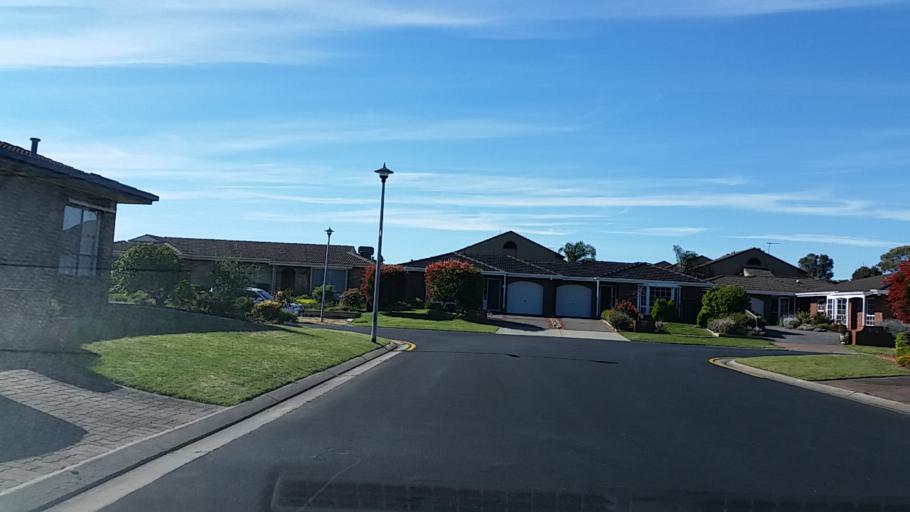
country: AU
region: South Australia
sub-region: Charles Sturt
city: West Lakes Shore
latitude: -34.8721
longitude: 138.4917
